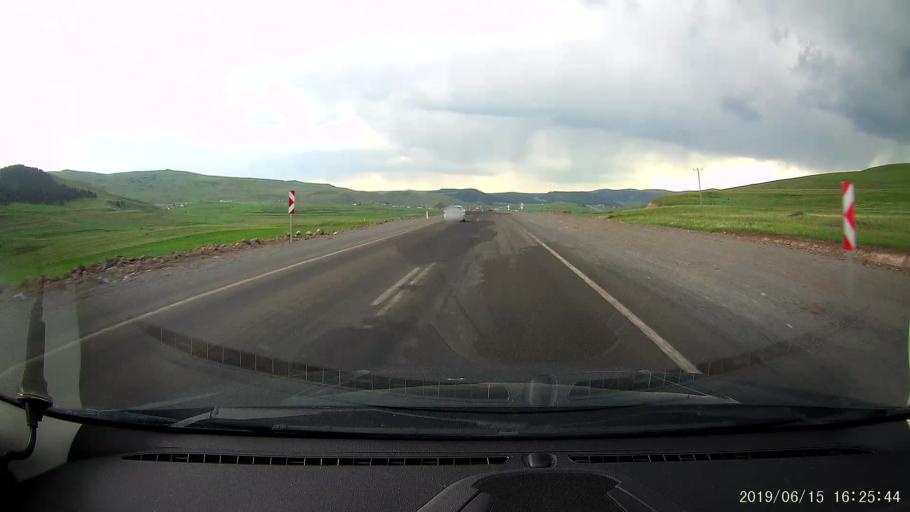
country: TR
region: Ardahan
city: Hanak
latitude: 41.1499
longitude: 42.8671
